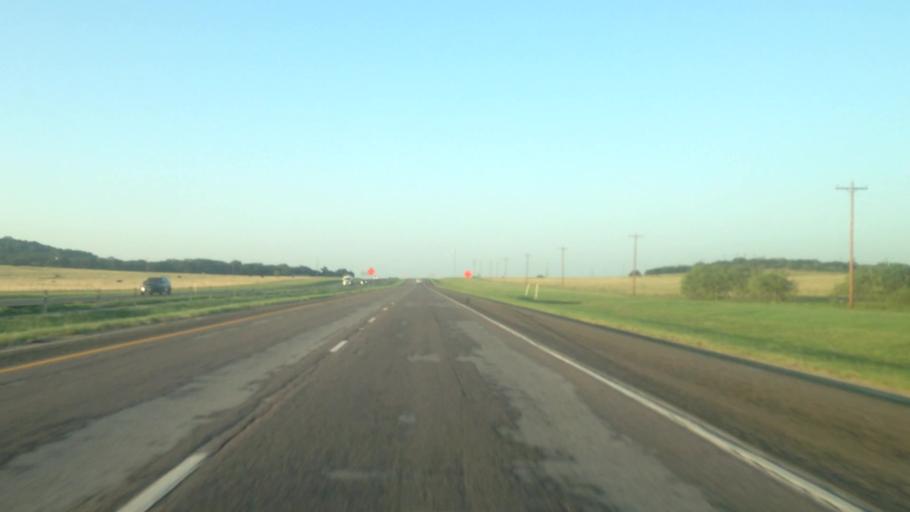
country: US
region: Texas
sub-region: Denton County
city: Argyle
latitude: 33.1408
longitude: -97.2003
